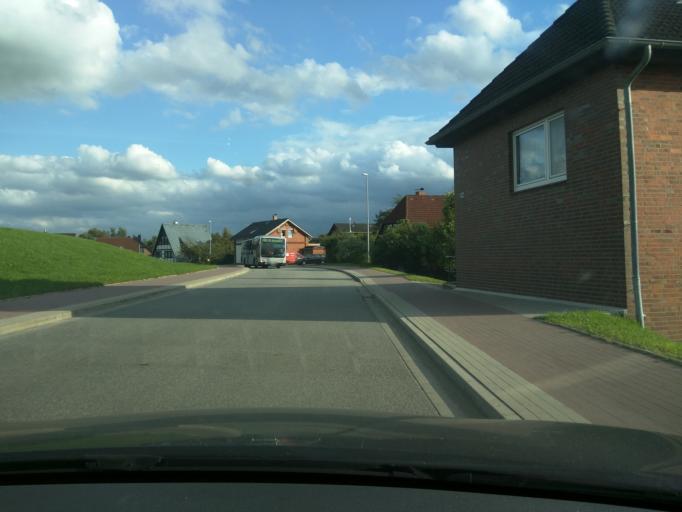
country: DE
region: Lower Saxony
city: Tespe
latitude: 53.3961
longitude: 10.4187
